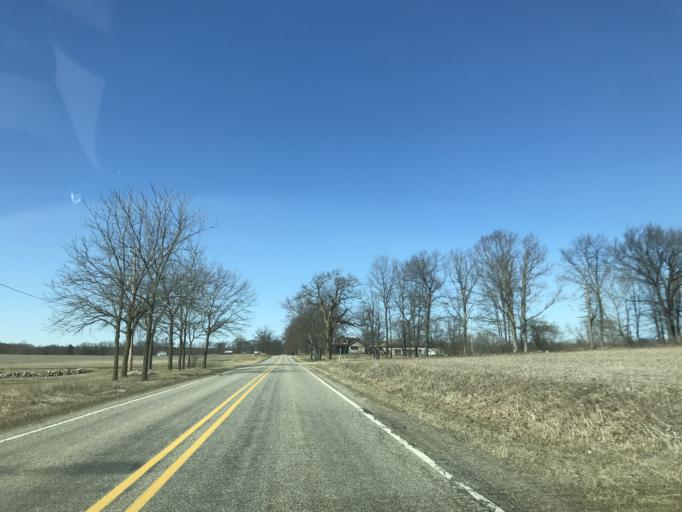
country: US
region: Michigan
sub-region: Hillsdale County
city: Litchfield
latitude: 41.9855
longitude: -84.7278
